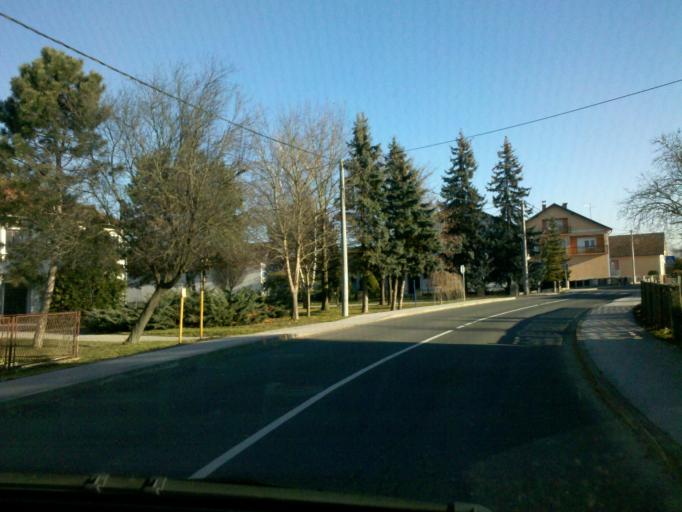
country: HR
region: Medimurska
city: Hodosan
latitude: 46.4090
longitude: 16.6215
